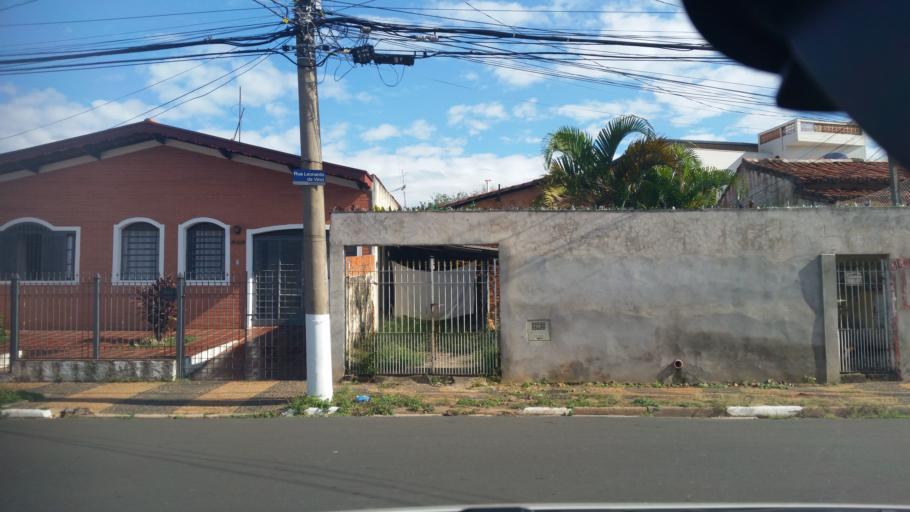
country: BR
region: Sao Paulo
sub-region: Campinas
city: Campinas
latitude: -22.8761
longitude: -47.0427
